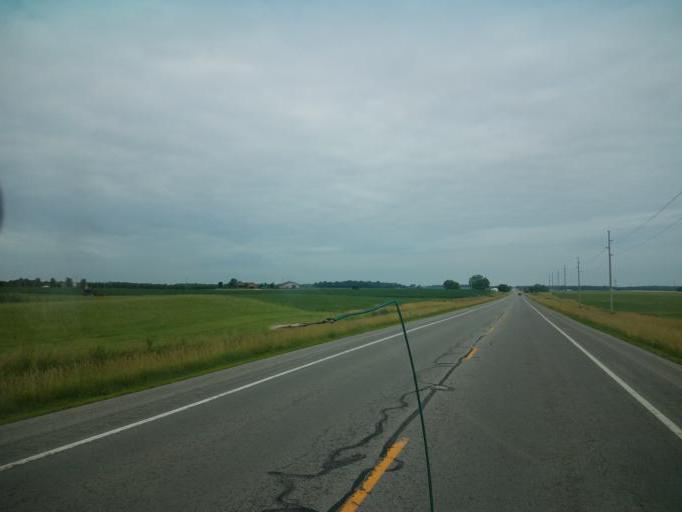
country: US
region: Ohio
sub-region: Hardin County
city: Kenton
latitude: 40.6636
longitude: -83.6498
